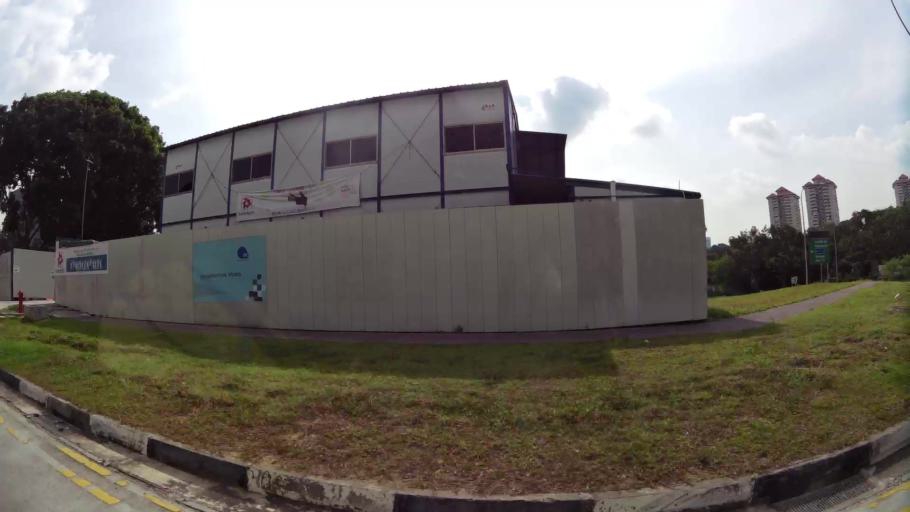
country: SG
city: Singapore
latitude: 1.2917
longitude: 103.7924
